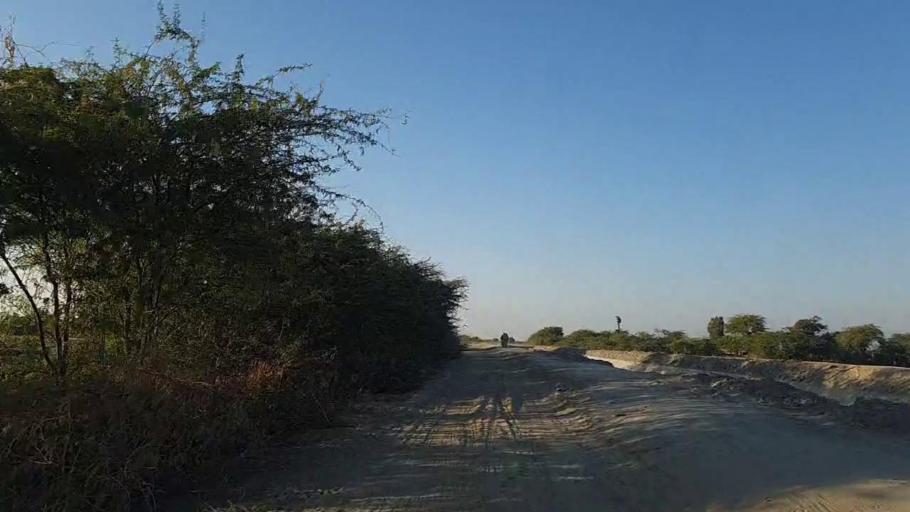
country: PK
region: Sindh
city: Naukot
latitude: 24.9959
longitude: 69.4000
